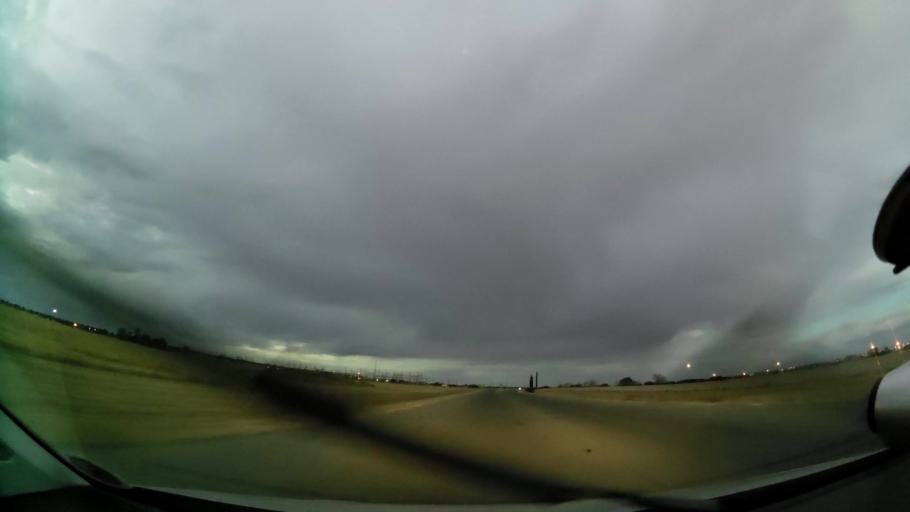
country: ZA
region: Orange Free State
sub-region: Lejweleputswa District Municipality
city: Welkom
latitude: -27.9512
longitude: 26.7920
